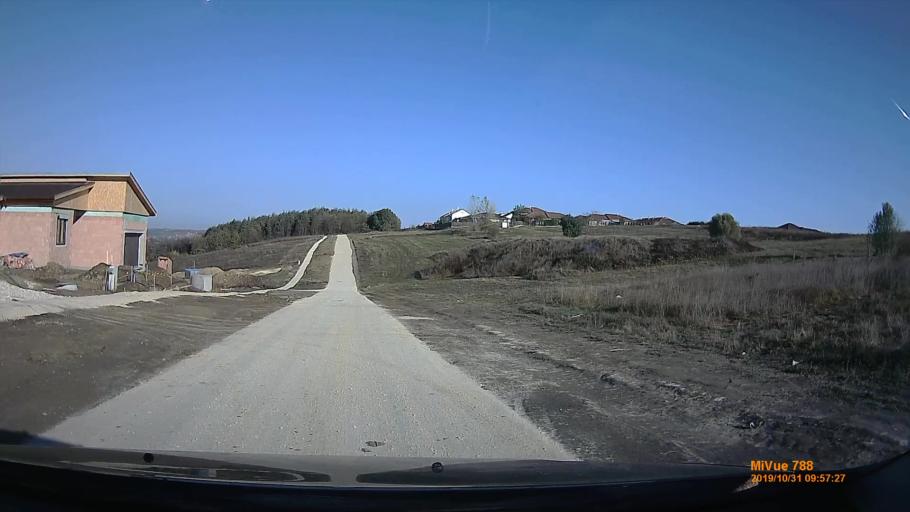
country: HU
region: Pest
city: Pecel
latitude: 47.4707
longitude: 19.3468
